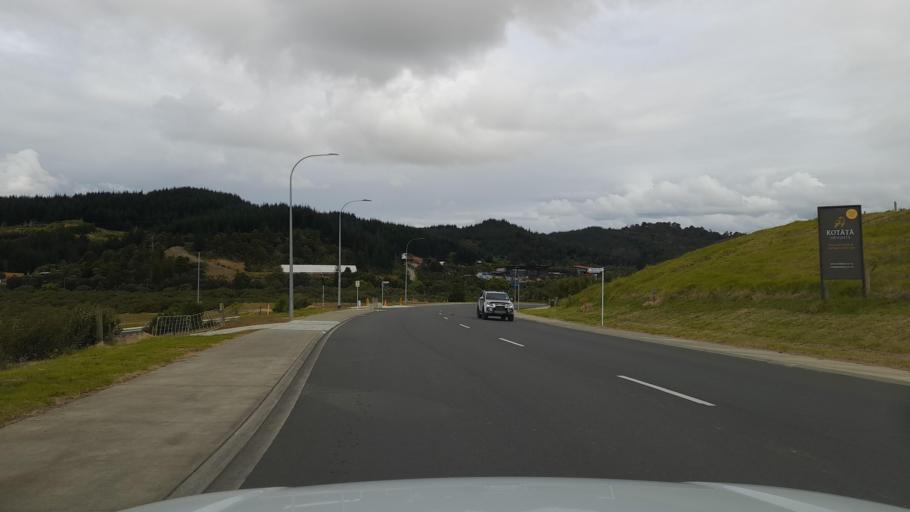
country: NZ
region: Northland
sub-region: Whangarei
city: Whangarei
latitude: -35.7448
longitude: 174.3178
